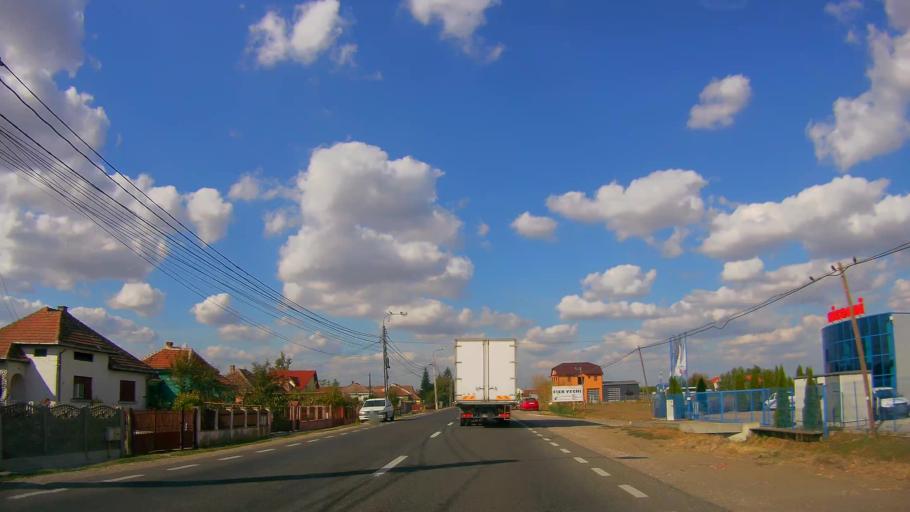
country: RO
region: Satu Mare
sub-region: Comuna Paulesti
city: Paulesti
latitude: 47.7509
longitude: 22.8831
